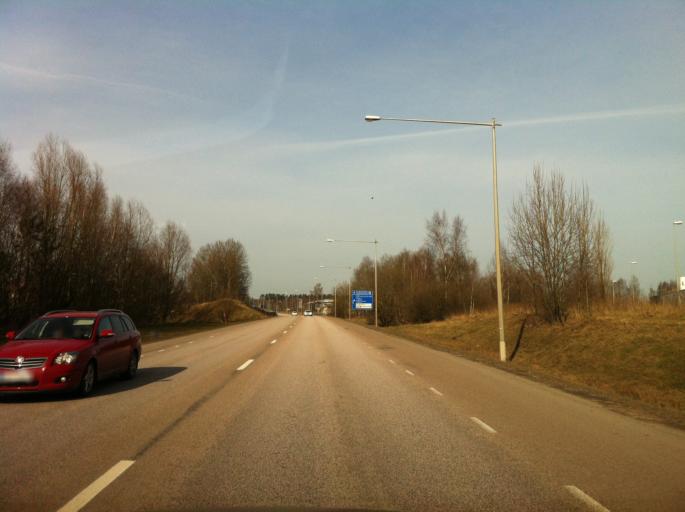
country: SE
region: Vaestra Goetaland
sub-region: Skovde Kommun
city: Skoevde
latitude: 58.3895
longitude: 13.8749
